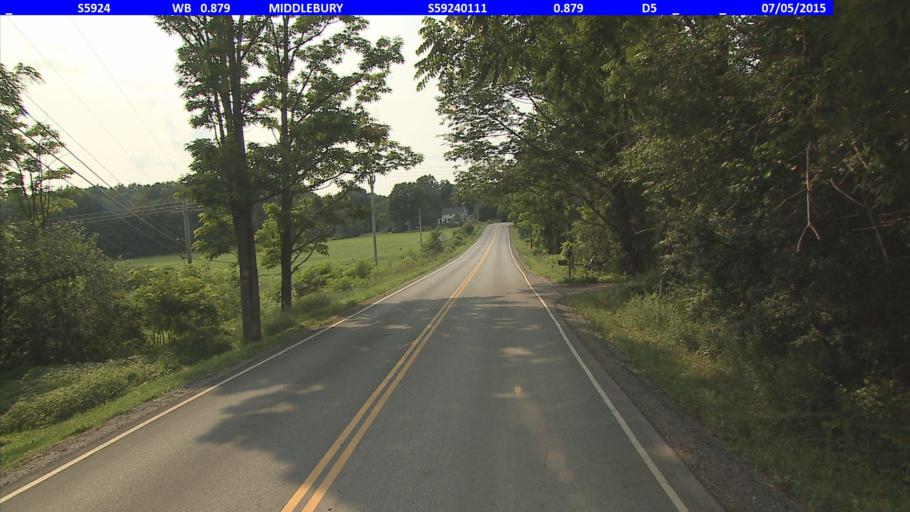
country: US
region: Vermont
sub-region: Addison County
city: Middlebury (village)
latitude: 44.0128
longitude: -73.1451
